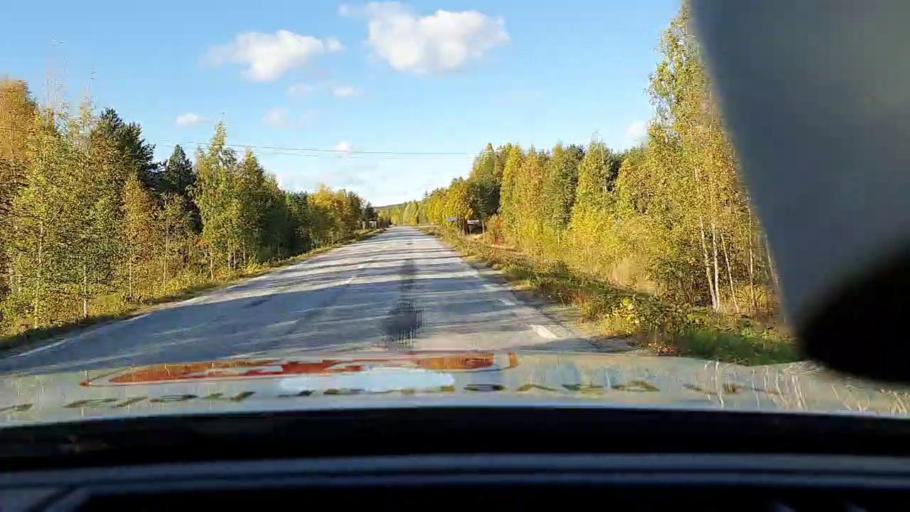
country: SE
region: Norrbotten
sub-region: Pitea Kommun
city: Norrfjarden
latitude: 65.4587
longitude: 21.4542
